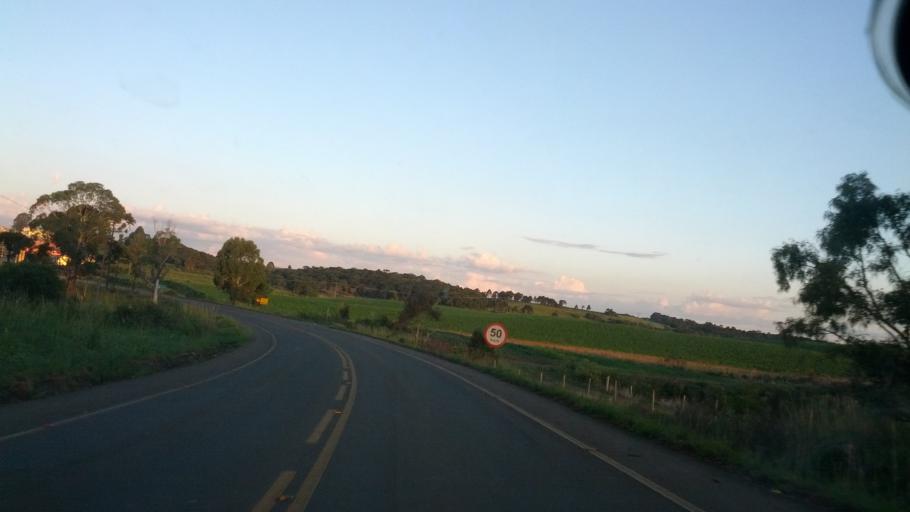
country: BR
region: Rio Grande do Sul
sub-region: Vacaria
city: Estrela
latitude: -27.7977
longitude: -50.8824
